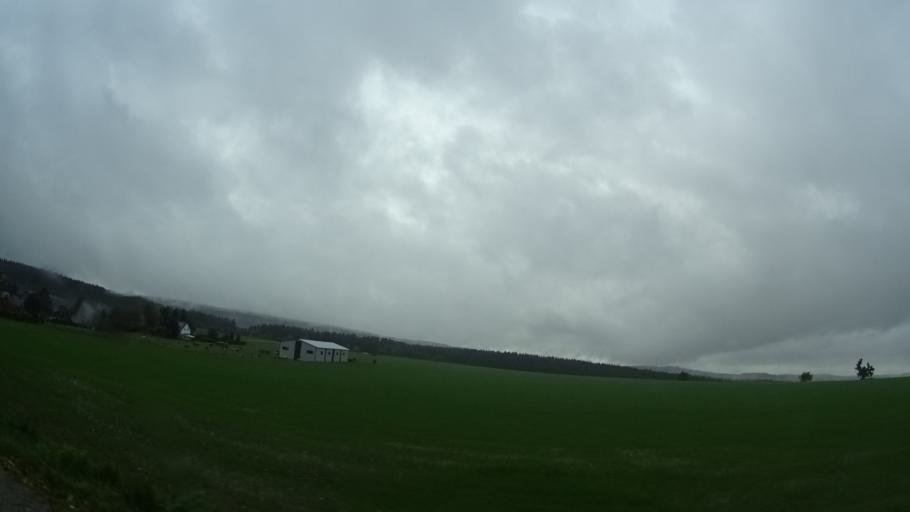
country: DE
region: Thuringia
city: Wurzbach
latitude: 50.4295
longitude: 11.5027
